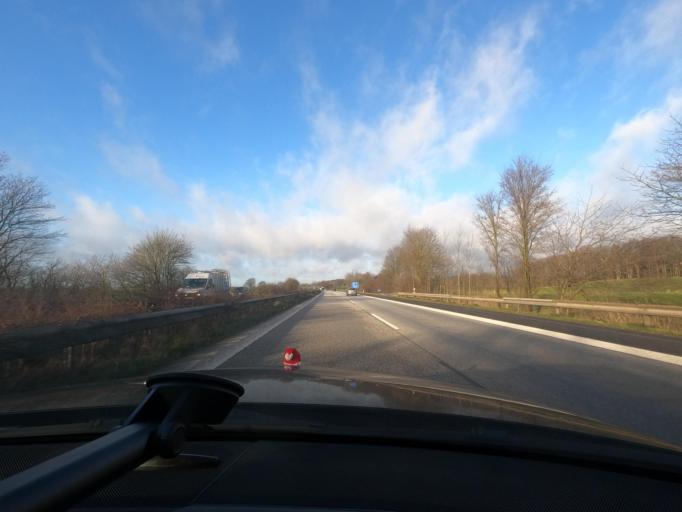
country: DE
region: Schleswig-Holstein
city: Alt Duvenstedt
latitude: 54.3915
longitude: 9.6508
